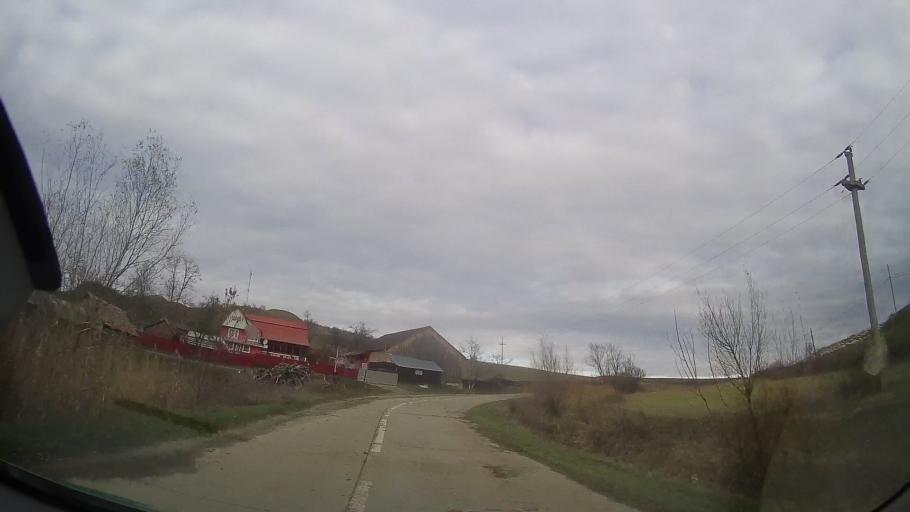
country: RO
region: Bistrita-Nasaud
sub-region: Comuna Micestii de Campie
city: Micestii de Campie
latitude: 46.8452
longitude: 24.3001
